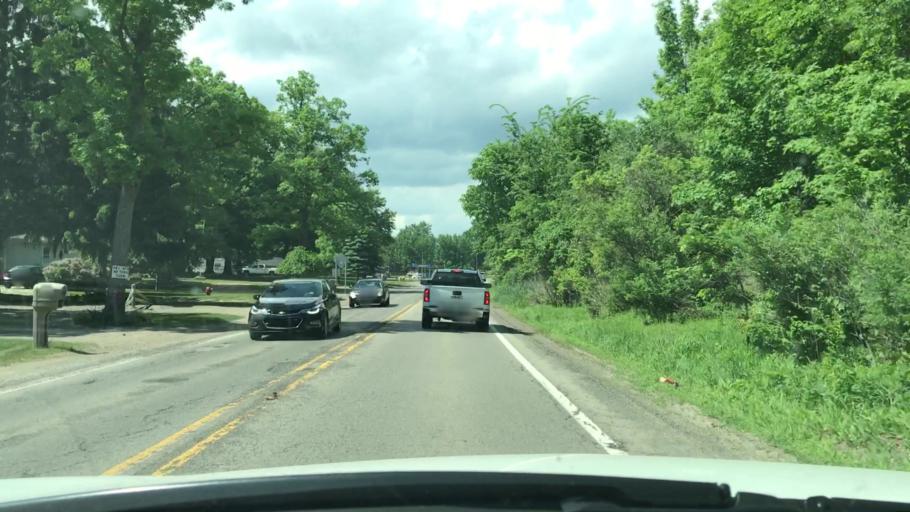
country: US
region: Michigan
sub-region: Oakland County
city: Auburn Hills
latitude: 42.7212
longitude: -83.2850
